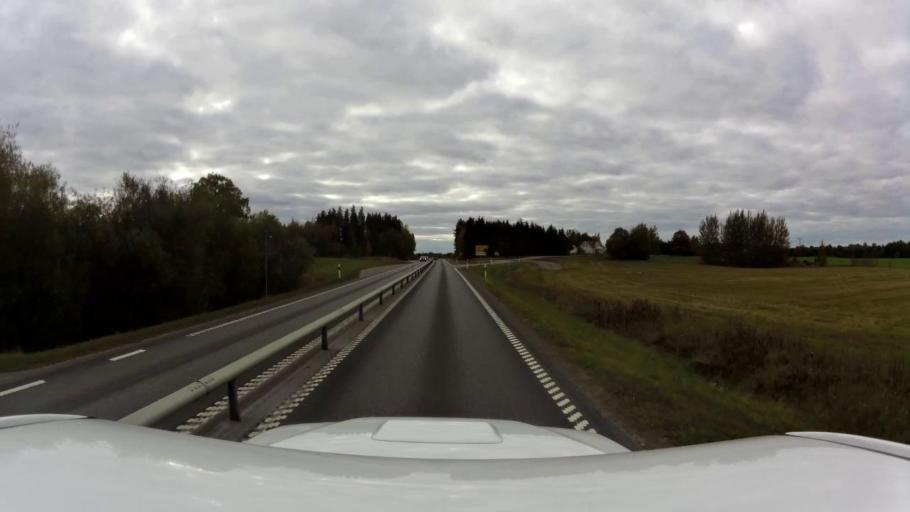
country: SE
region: OEstergoetland
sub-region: Linkopings Kommun
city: Malmslatt
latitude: 58.3591
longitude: 15.5456
